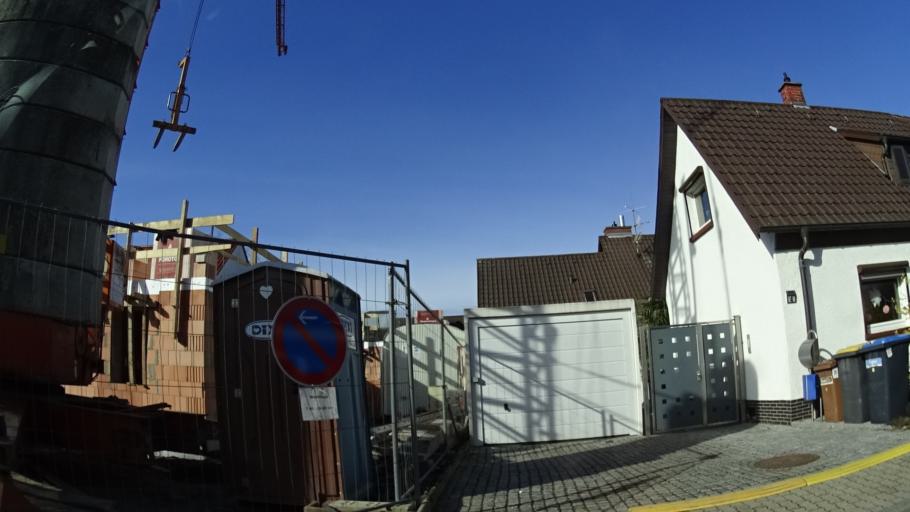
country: DE
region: Baden-Wuerttemberg
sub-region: Karlsruhe Region
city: Eppelheim
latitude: 49.3994
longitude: 8.6457
